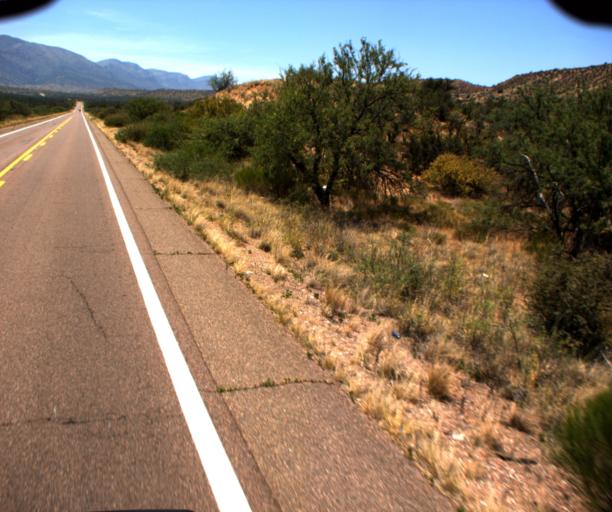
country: US
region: Arizona
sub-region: Gila County
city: Tonto Basin
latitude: 34.0173
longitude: -111.3304
